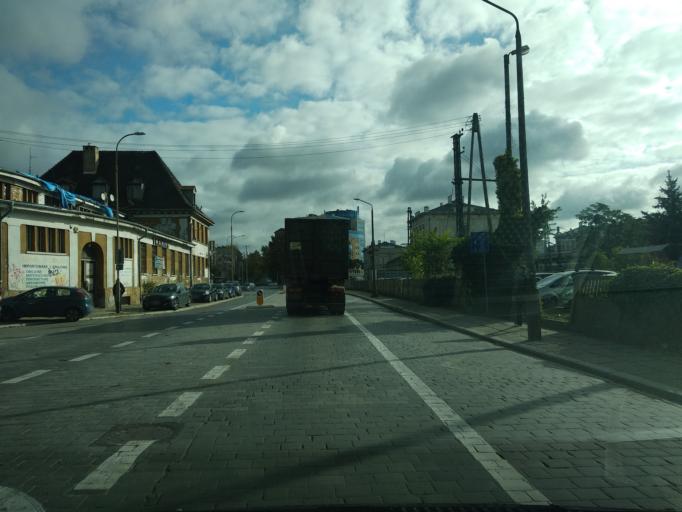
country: PL
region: Lower Silesian Voivodeship
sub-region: Powiat wroclawski
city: Wroclaw
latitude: 51.1082
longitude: 17.0163
